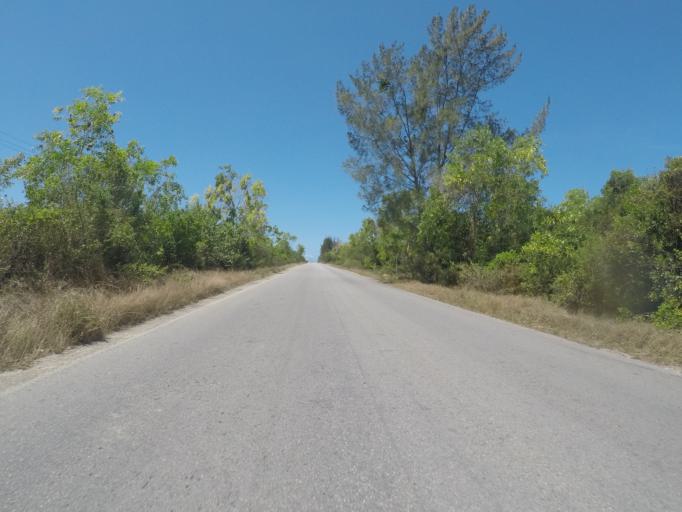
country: TZ
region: Zanzibar Central/South
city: Nganane
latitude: -6.2689
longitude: 39.5160
